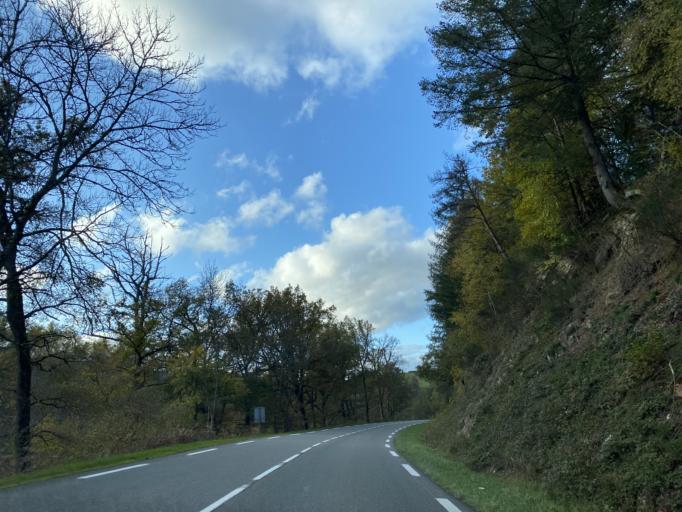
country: FR
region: Auvergne
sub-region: Departement du Puy-de-Dome
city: Job
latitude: 45.6462
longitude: 3.6810
